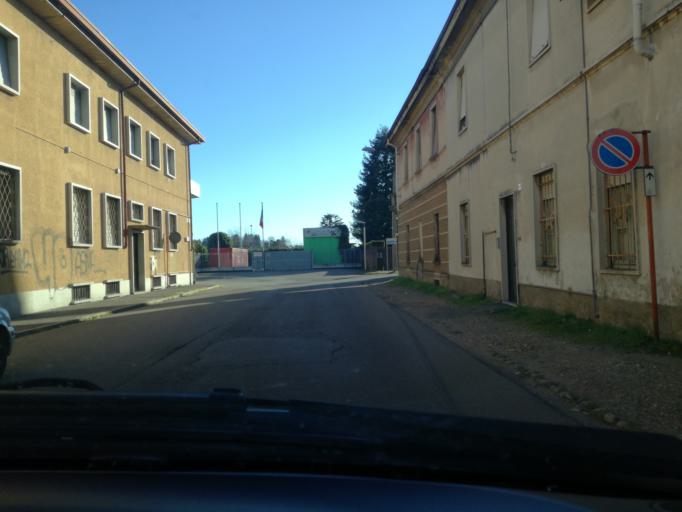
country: IT
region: Lombardy
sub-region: Provincia di Varese
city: Gallarate
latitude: 45.6719
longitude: 8.7987
